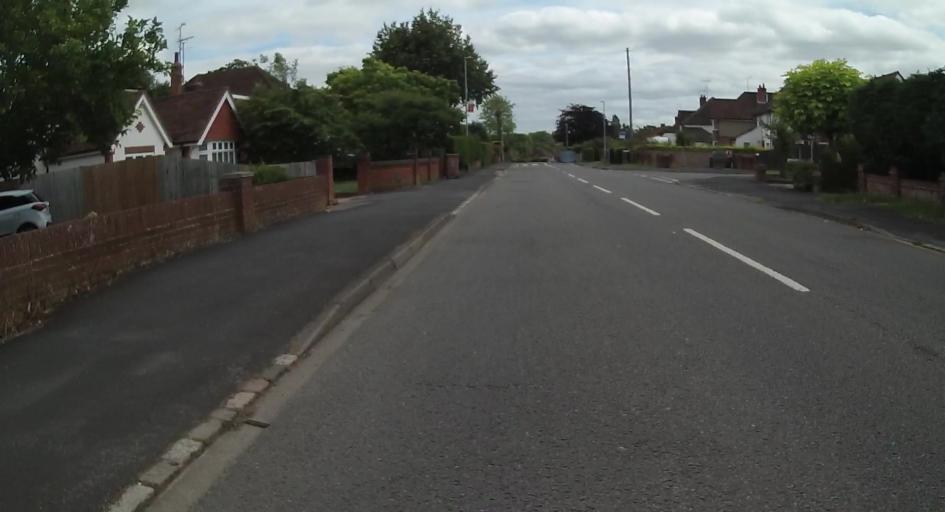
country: GB
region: England
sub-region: Wokingham
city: Earley
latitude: 51.4351
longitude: -0.9326
